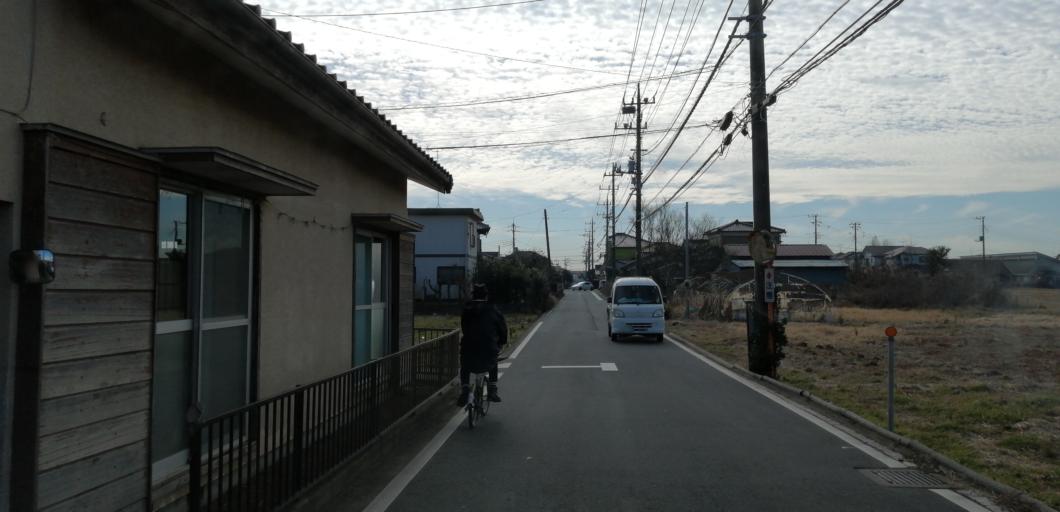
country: JP
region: Chiba
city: Narita
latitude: 35.7429
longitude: 140.3320
